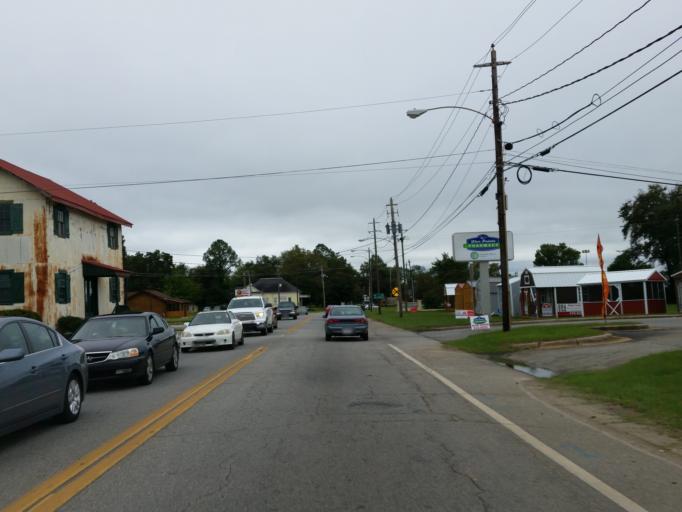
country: US
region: Georgia
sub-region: Peach County
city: Fort Valley
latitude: 32.5557
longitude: -83.8836
